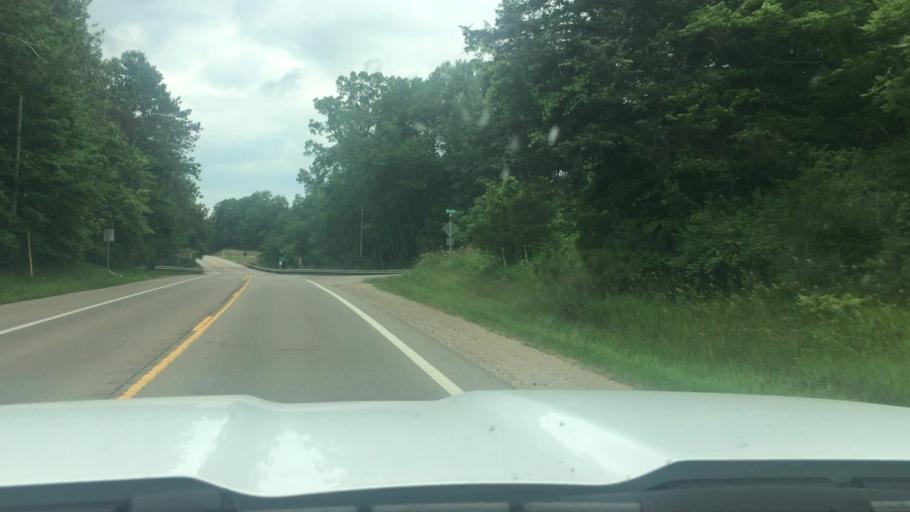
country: US
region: Michigan
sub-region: Ionia County
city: Portland
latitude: 43.0015
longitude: -84.9245
